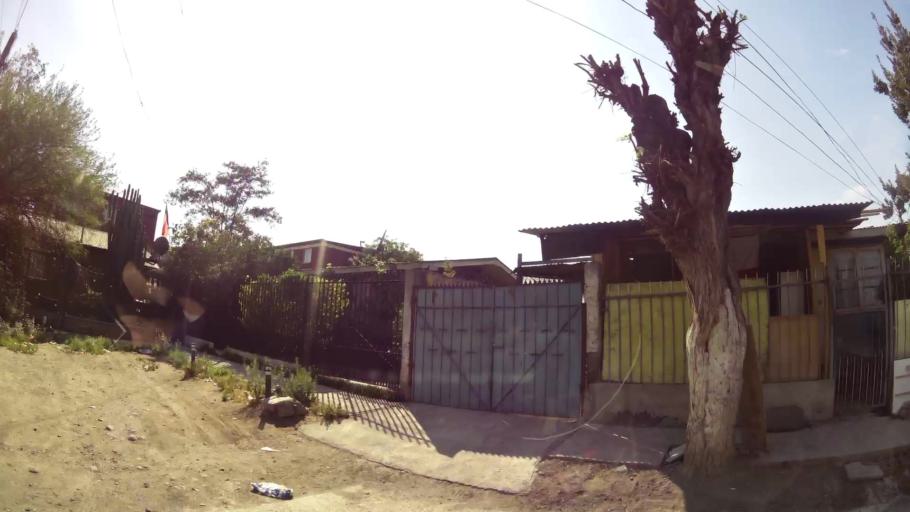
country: CL
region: Santiago Metropolitan
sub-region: Provincia de Santiago
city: La Pintana
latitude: -33.5585
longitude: -70.6692
